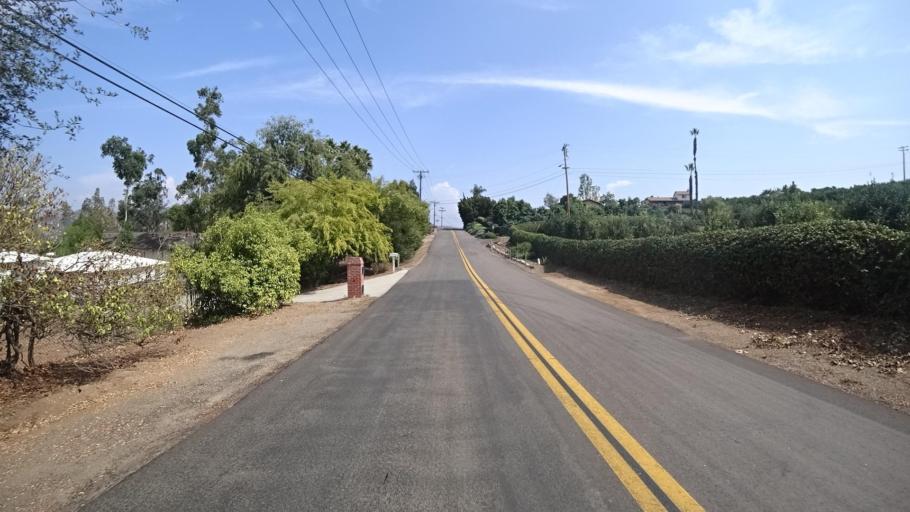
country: US
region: California
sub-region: San Diego County
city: Escondido
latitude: 33.1237
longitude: -117.0265
